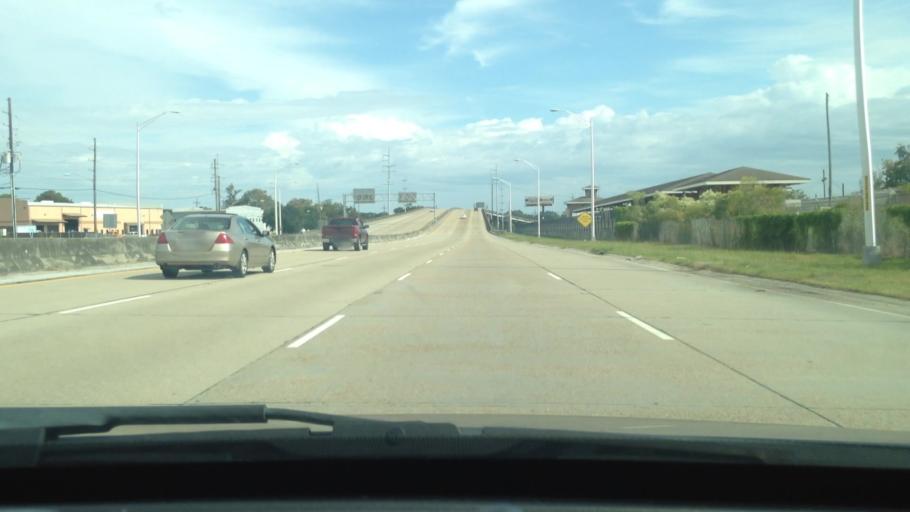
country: US
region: Louisiana
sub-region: Jefferson Parish
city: Metairie Terrace
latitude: 29.9690
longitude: -90.1777
